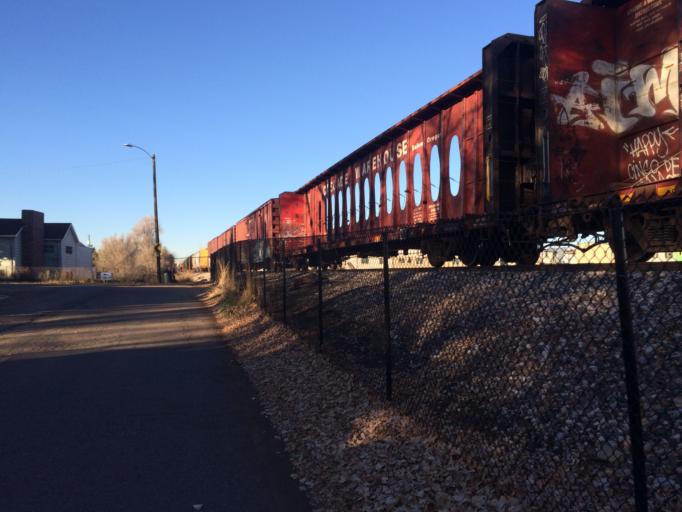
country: US
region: Colorado
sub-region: Boulder County
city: Louisville
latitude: 39.9814
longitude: -105.1309
